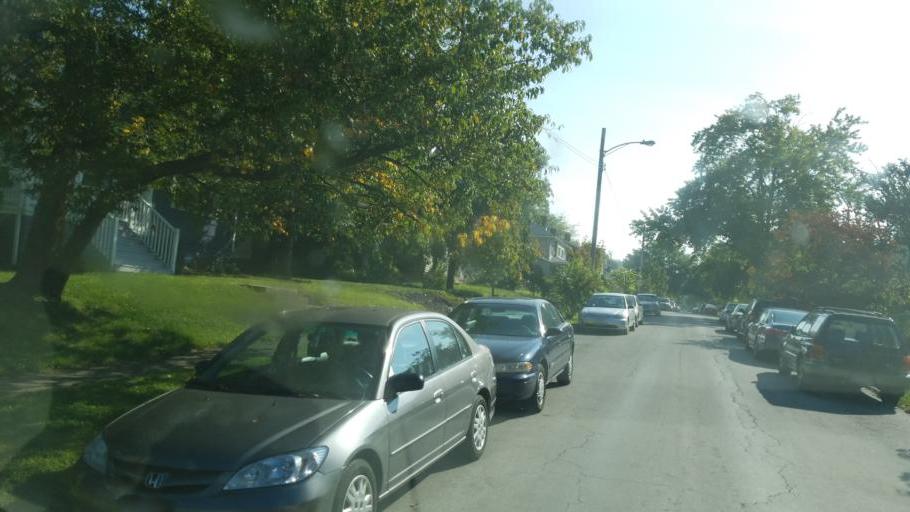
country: US
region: Ohio
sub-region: Franklin County
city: Grandview Heights
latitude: 40.0217
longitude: -83.0124
